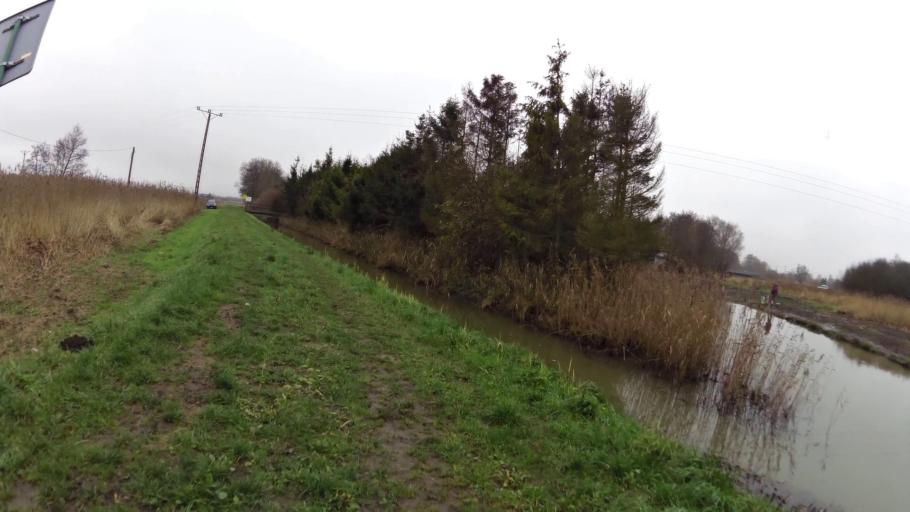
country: PL
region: West Pomeranian Voivodeship
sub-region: Powiat koszalinski
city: Mielno
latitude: 54.2450
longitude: 16.0821
